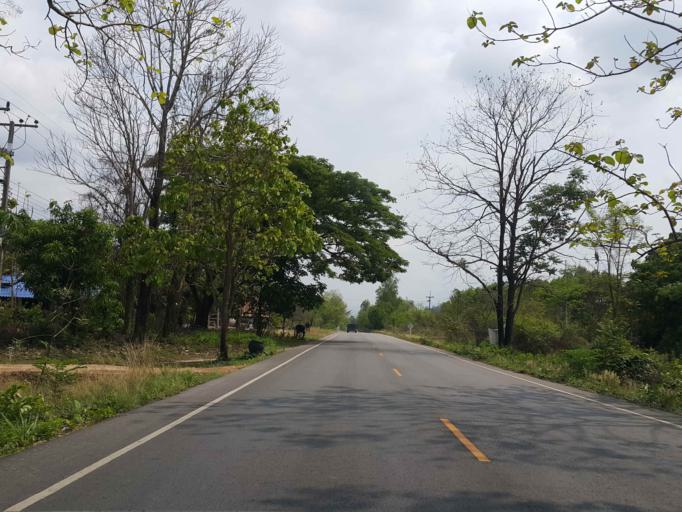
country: TH
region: Lampang
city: Thoen
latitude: 17.5005
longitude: 99.3503
